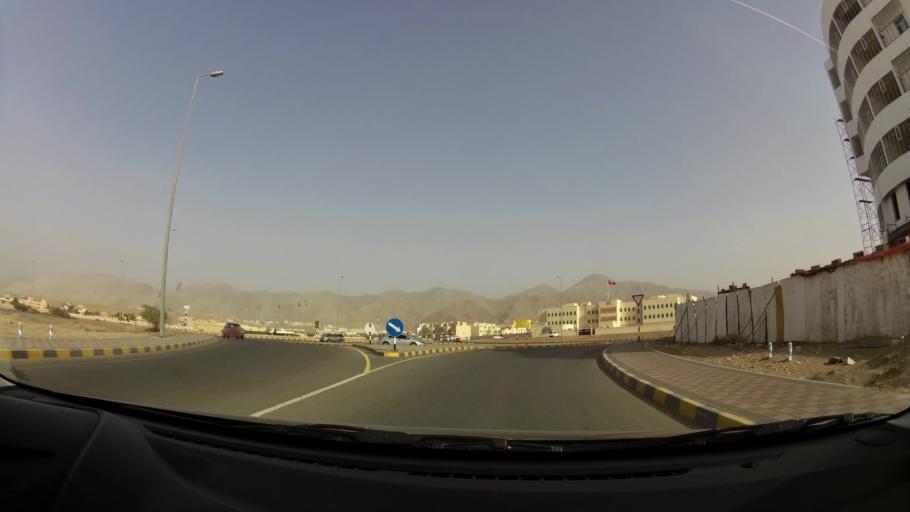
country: OM
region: Muhafazat Masqat
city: Bawshar
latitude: 23.5486
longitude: 58.3628
